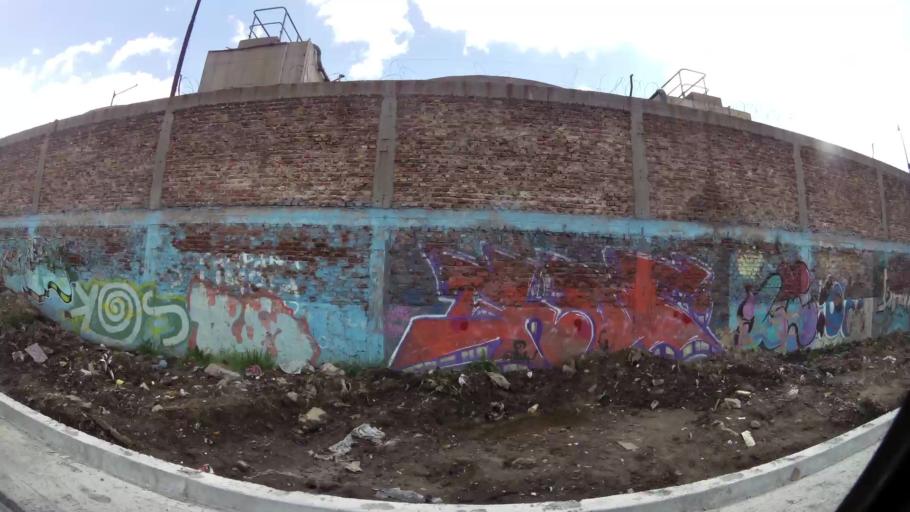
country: AR
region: Buenos Aires F.D.
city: Villa Lugano
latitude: -34.6869
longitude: -58.4404
